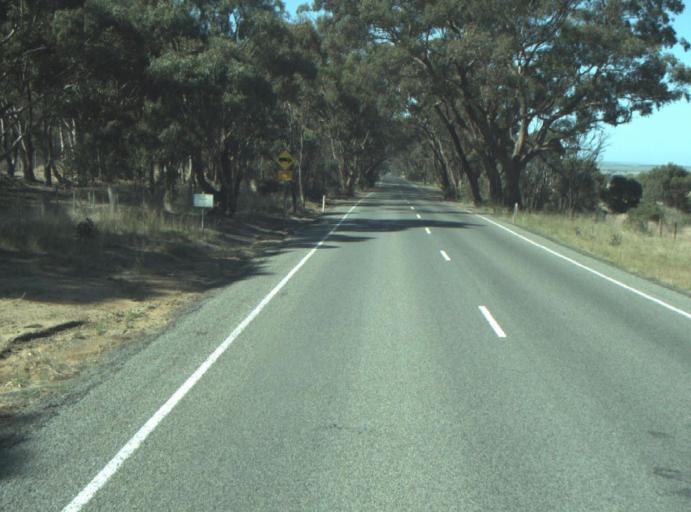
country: AU
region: Victoria
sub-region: Greater Geelong
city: Lara
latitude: -37.9160
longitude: 144.3974
